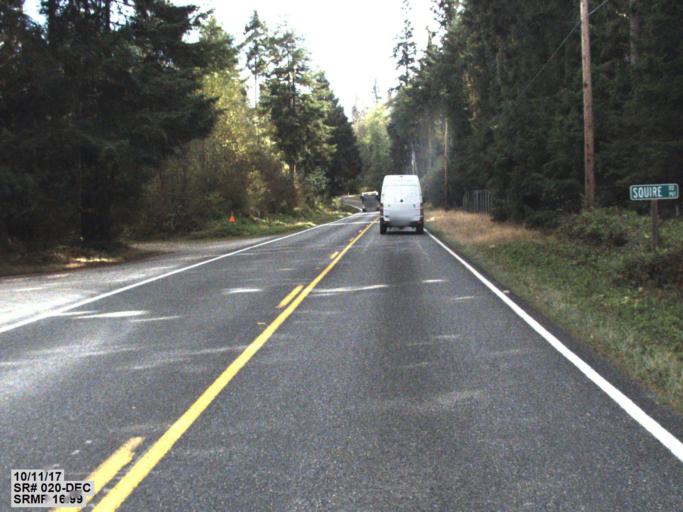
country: US
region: Washington
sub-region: Island County
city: Coupeville
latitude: 48.1775
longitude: -122.6183
